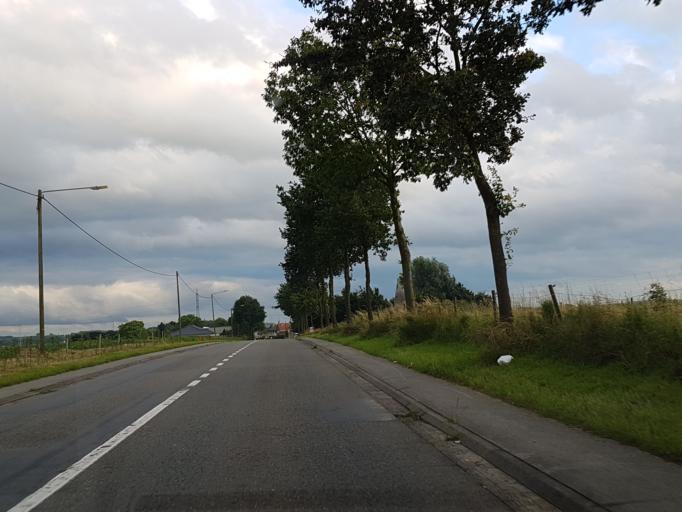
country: BE
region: Flanders
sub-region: Provincie Vlaams-Brabant
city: Merchtem
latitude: 50.9769
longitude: 4.2308
